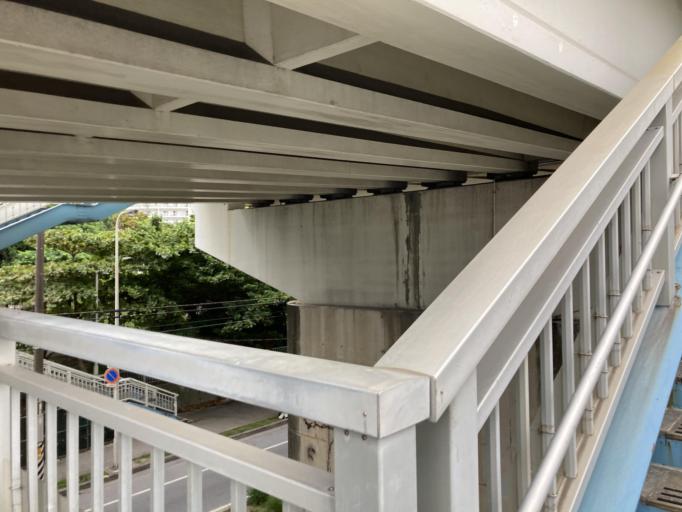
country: JP
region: Okinawa
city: Naha-shi
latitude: 26.2296
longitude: 127.6814
